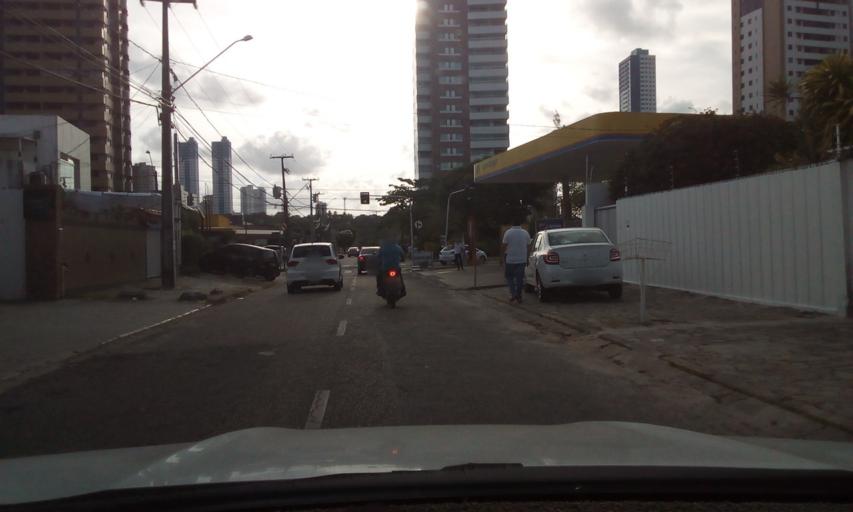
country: BR
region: Paraiba
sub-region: Joao Pessoa
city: Joao Pessoa
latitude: -7.1024
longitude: -34.8369
